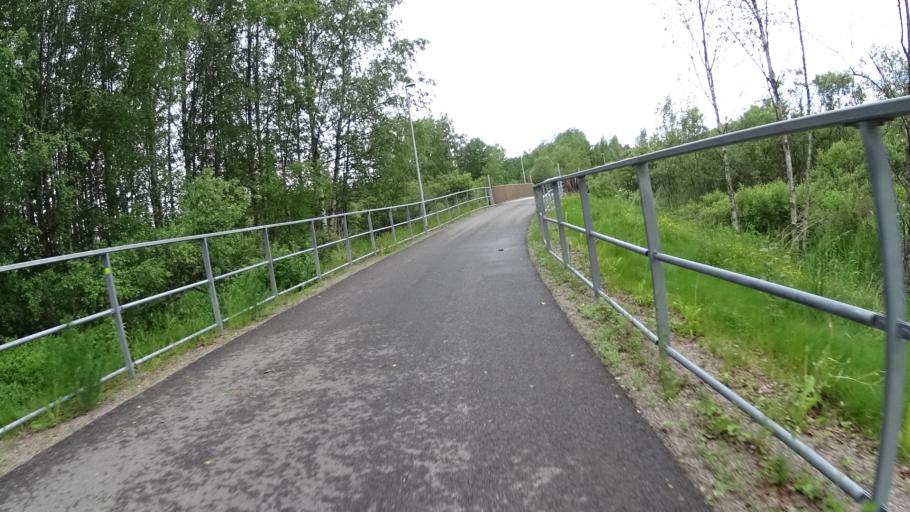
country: FI
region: Uusimaa
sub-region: Helsinki
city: Kilo
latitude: 60.2723
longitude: 24.7836
